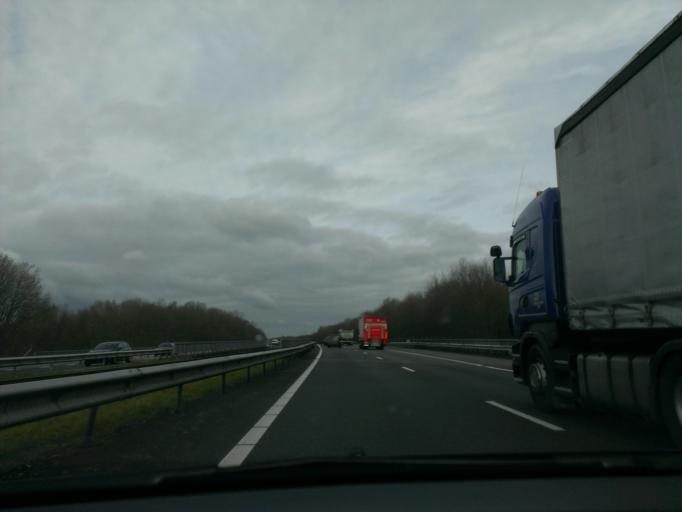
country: NL
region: Overijssel
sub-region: Gemeente Almelo
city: Almelo
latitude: 52.3144
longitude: 6.6891
